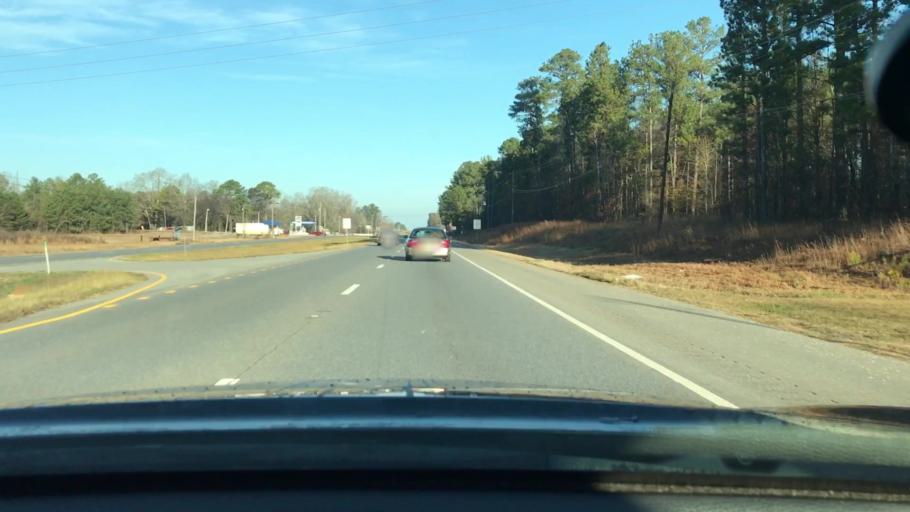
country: US
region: Alabama
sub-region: Talladega County
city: Childersburg
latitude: 33.2385
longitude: -86.3319
